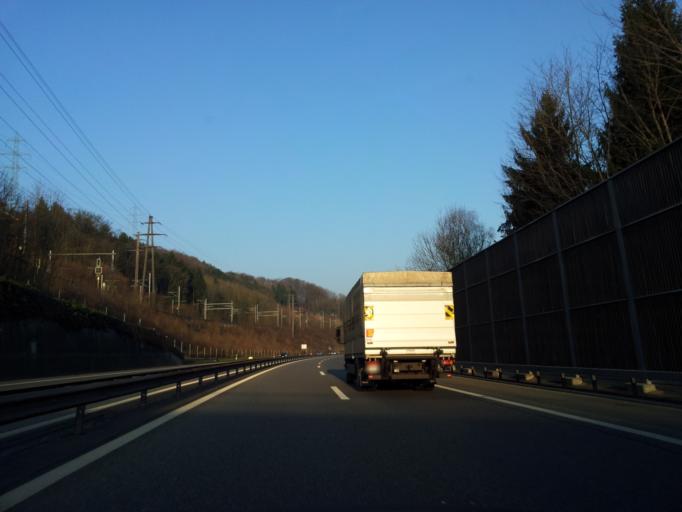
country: CH
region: Aargau
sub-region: Bezirk Rheinfelden
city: Mumpf
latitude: 47.5447
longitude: 7.9191
